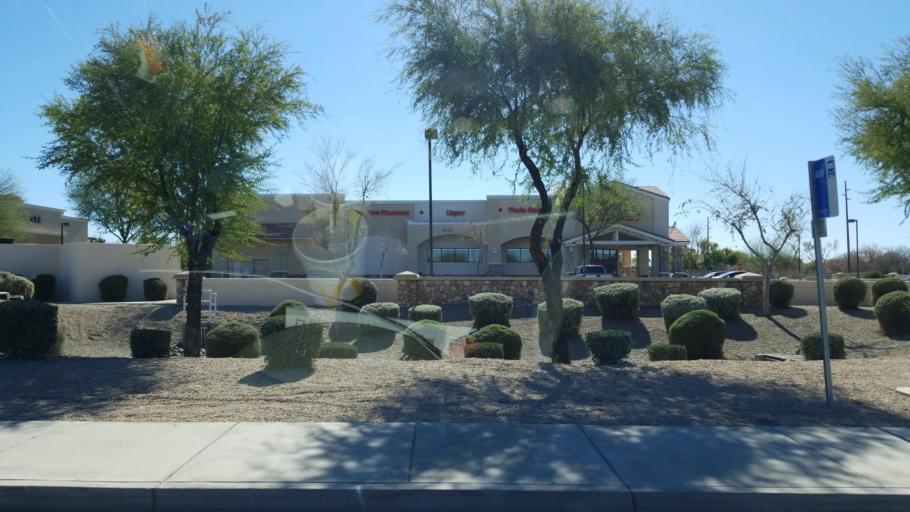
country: US
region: Arizona
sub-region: Maricopa County
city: Chandler
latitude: 33.3206
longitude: -111.8233
